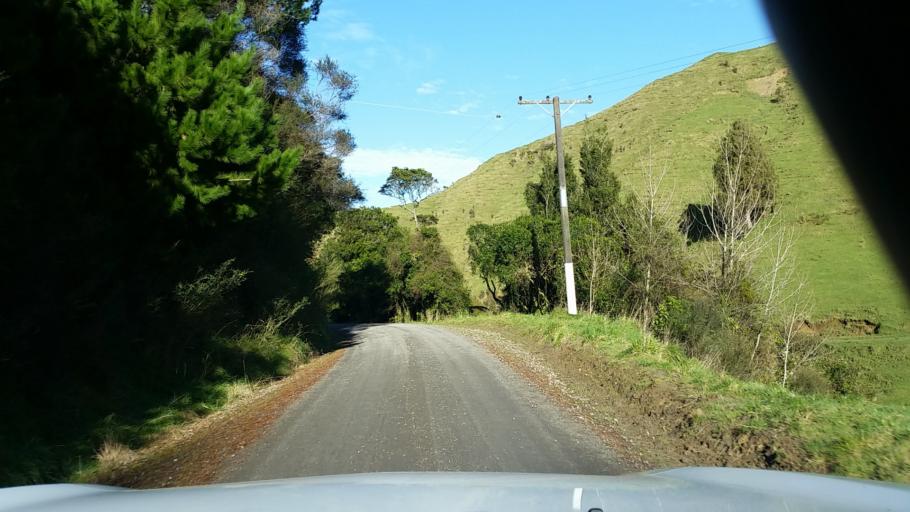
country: NZ
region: Taranaki
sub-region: South Taranaki District
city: Eltham
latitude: -39.5079
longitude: 174.3974
